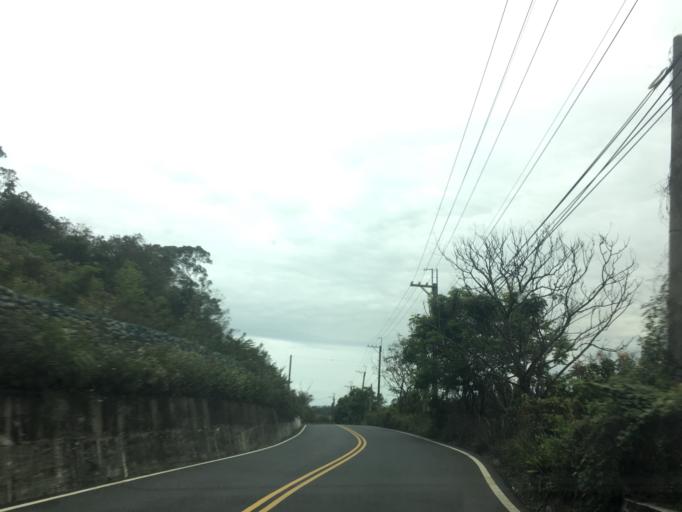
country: TW
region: Taiwan
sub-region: Taitung
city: Taitung
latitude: 22.8140
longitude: 121.1386
